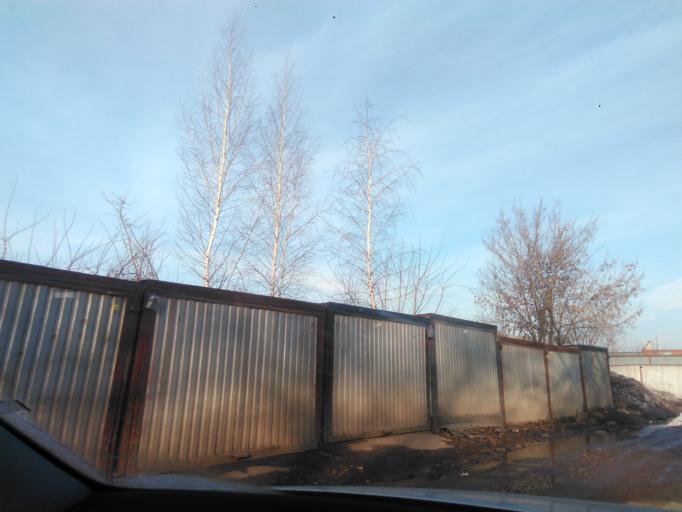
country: RU
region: Moscow
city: Zapadnoye Degunino
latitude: 55.8671
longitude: 37.5226
